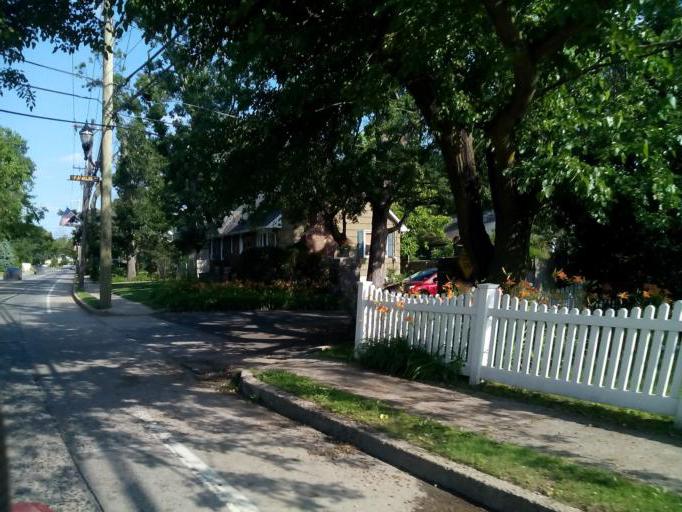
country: US
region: New York
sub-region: Nassau County
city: Bayville
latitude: 40.9090
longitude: -73.5567
